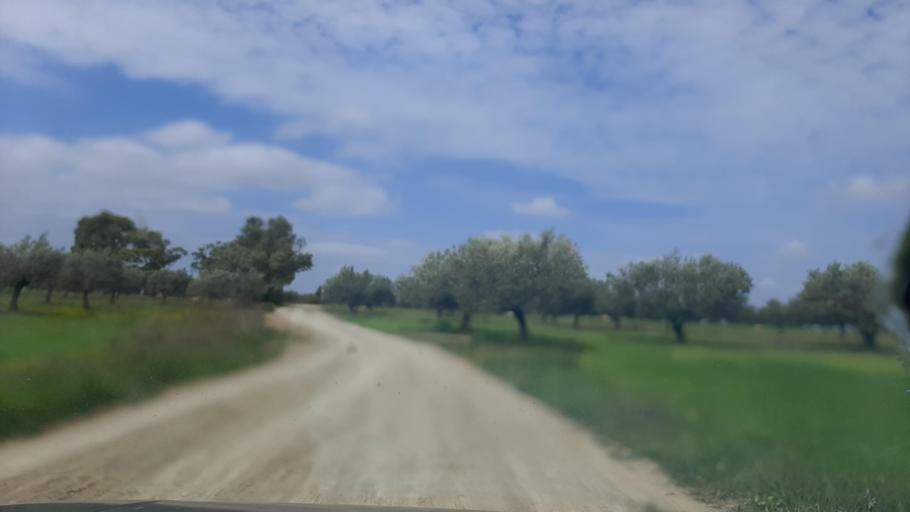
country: TN
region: Tunis
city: Oued Lill
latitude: 36.6887
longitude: 9.9951
